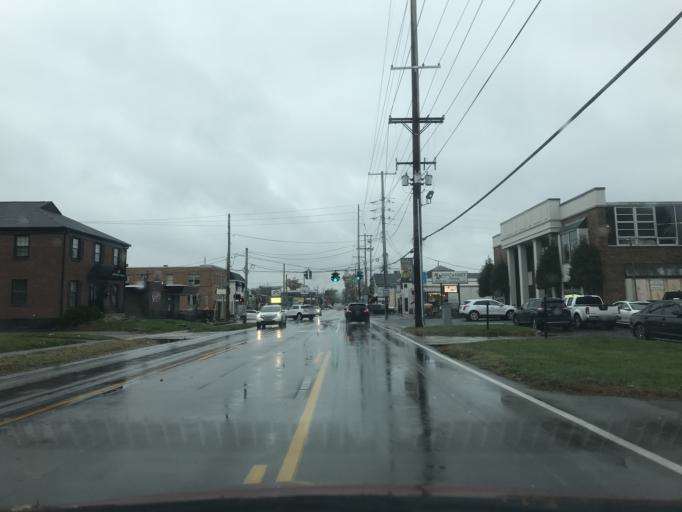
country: US
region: Kentucky
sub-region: Jefferson County
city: Saint Matthews
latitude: 38.2509
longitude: -85.6538
